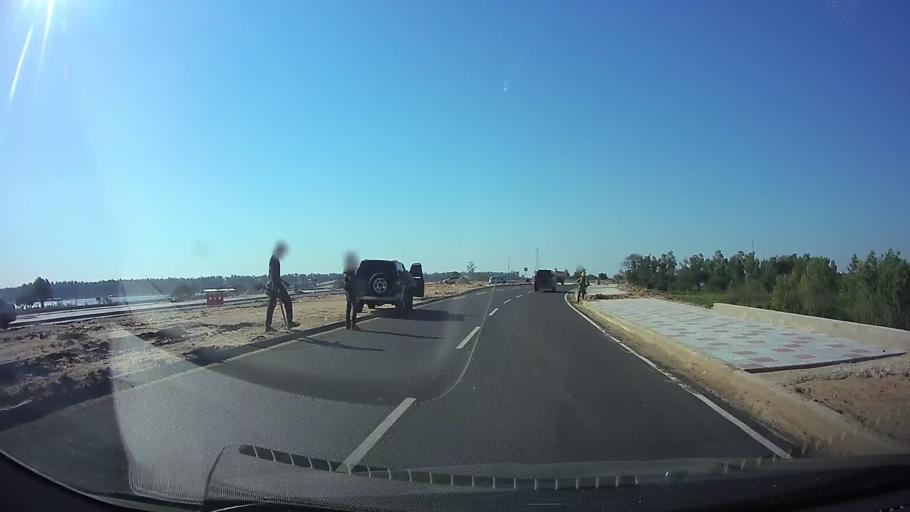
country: PY
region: Asuncion
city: Asuncion
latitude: -25.2530
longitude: -57.6060
